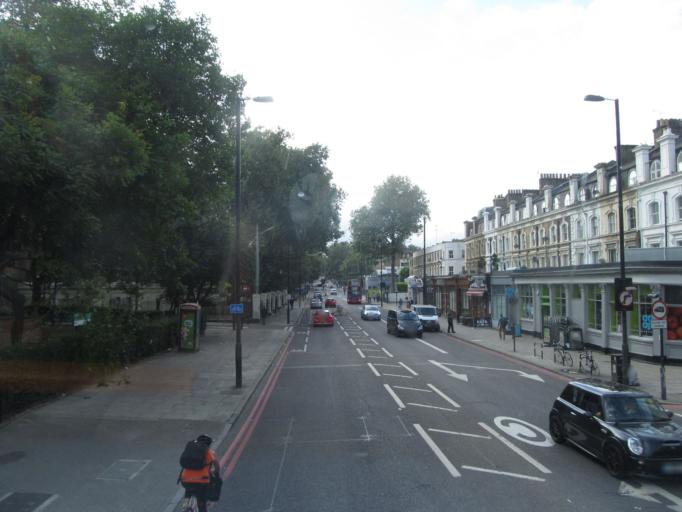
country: GB
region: England
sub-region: Greater London
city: Islington
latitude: 51.5298
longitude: -0.0978
